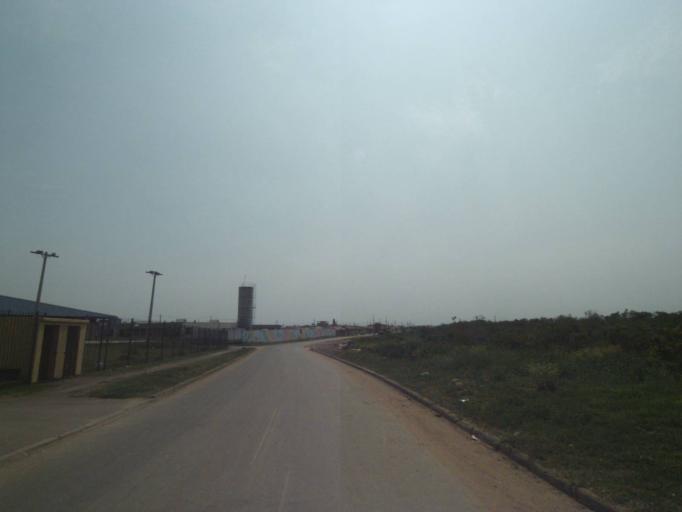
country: BR
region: Parana
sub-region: Sao Jose Dos Pinhais
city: Sao Jose dos Pinhais
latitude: -25.4975
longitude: -49.2004
